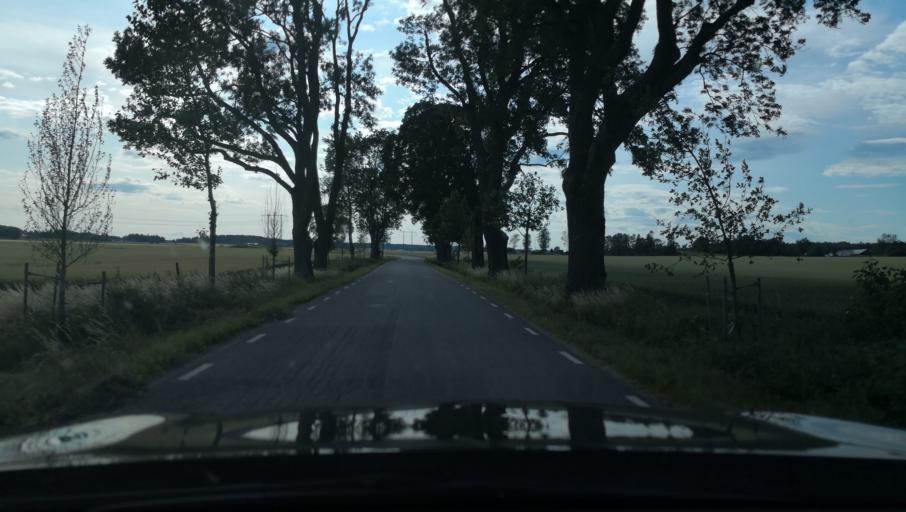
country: SE
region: Uppsala
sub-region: Enkopings Kommun
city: Orsundsbro
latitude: 59.6977
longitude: 17.3193
